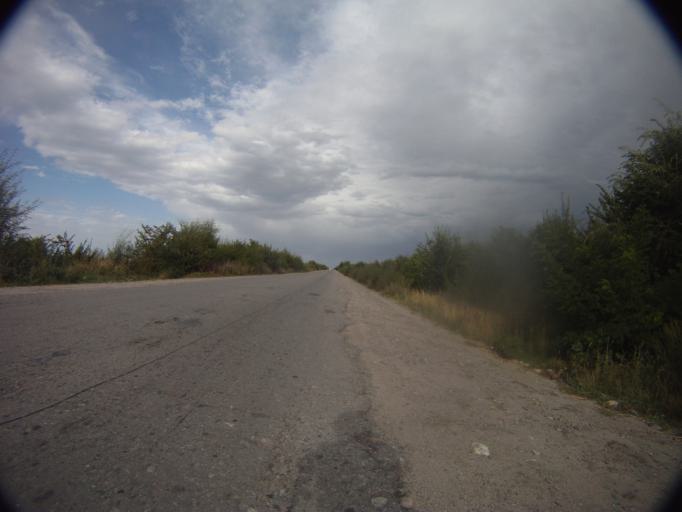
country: KG
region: Ysyk-Koel
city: Pokrovka
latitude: 42.2896
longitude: 77.8169
